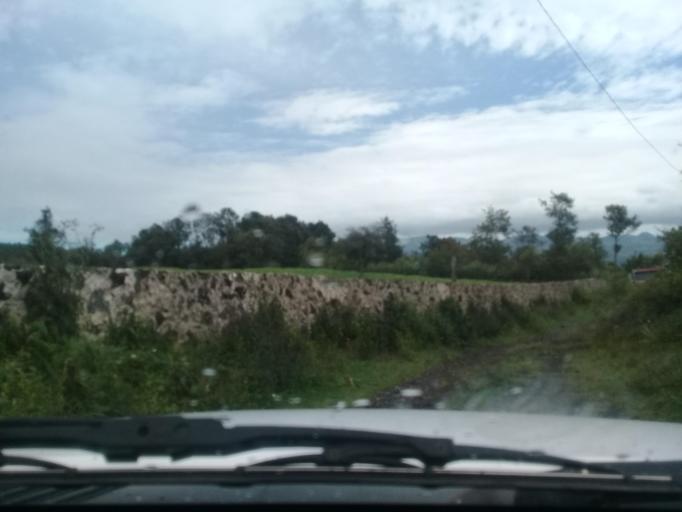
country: MX
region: Veracruz
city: Rafael Lucio
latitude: 19.6168
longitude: -96.9986
